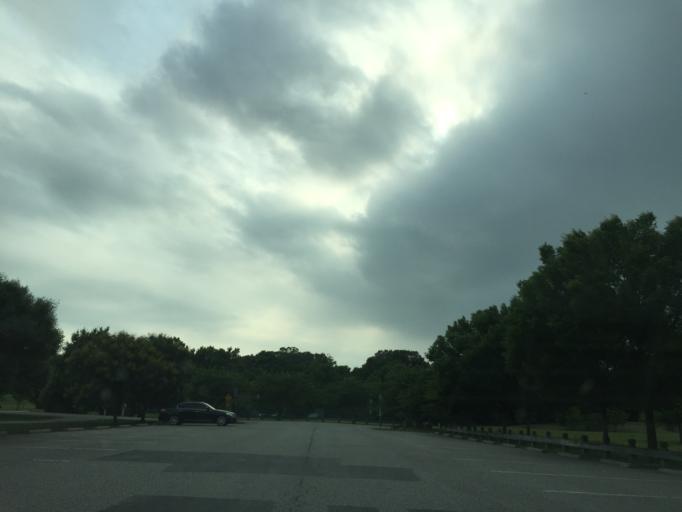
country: US
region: Virginia
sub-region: Isle of Wight County
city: Carrollton
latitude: 37.0910
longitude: -76.5309
